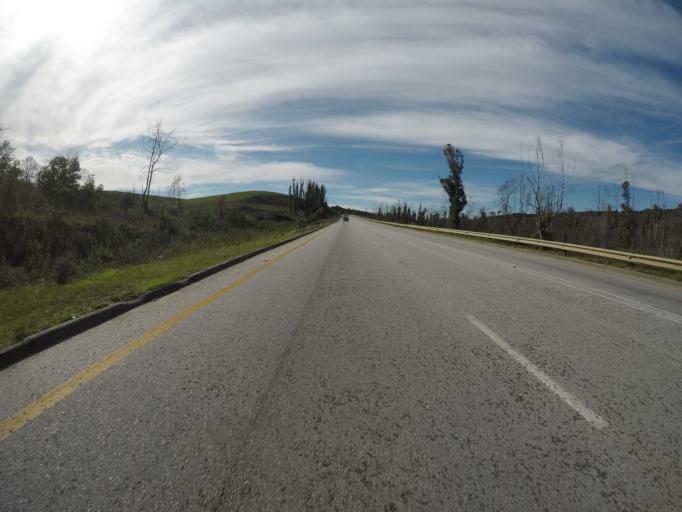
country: ZA
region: Eastern Cape
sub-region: Cacadu District Municipality
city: Jeffrey's Bay
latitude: -33.9032
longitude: 25.1045
